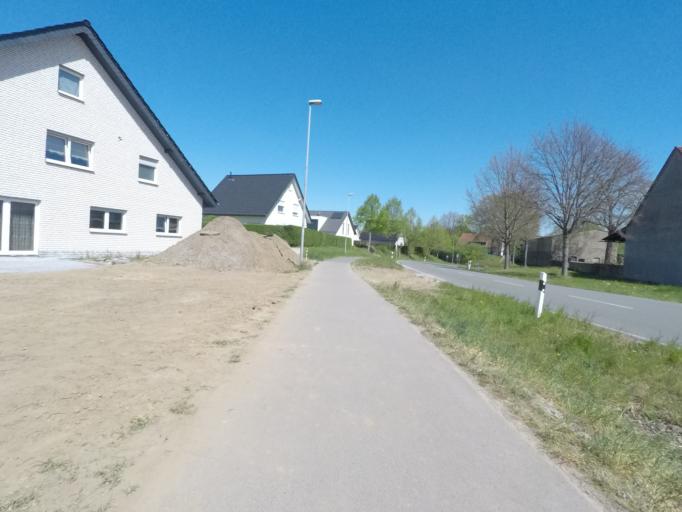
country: DE
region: North Rhine-Westphalia
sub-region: Regierungsbezirk Detmold
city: Herford
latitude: 52.0870
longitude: 8.6915
